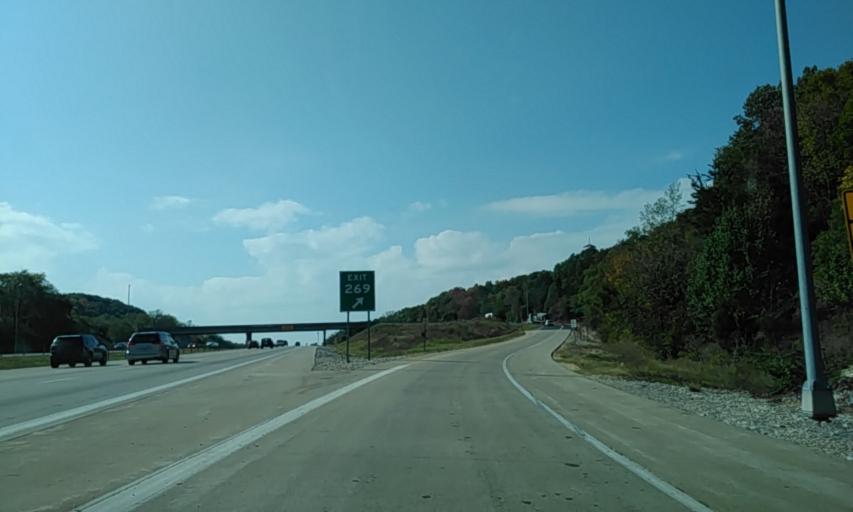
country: US
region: Missouri
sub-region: Jefferson County
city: High Ridge
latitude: 38.5174
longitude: -90.5482
